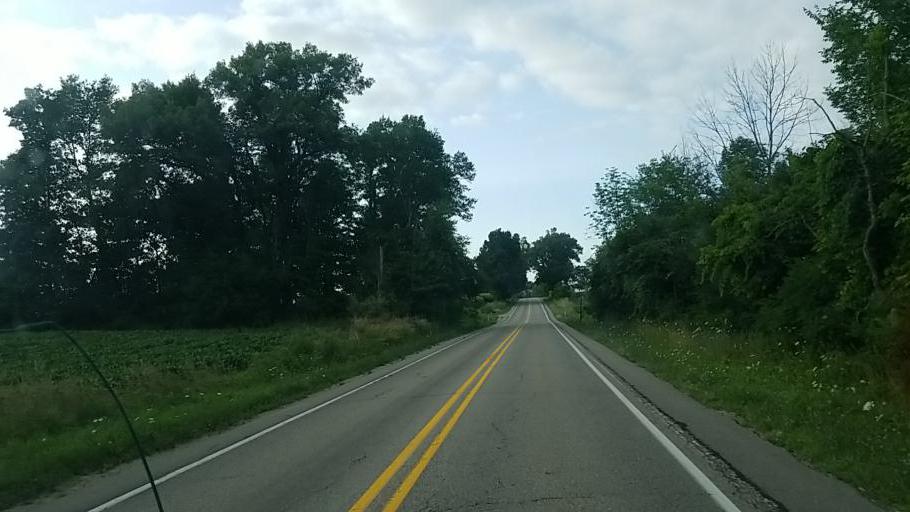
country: US
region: Michigan
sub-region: Montcalm County
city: Greenville
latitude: 43.1051
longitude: -85.3526
